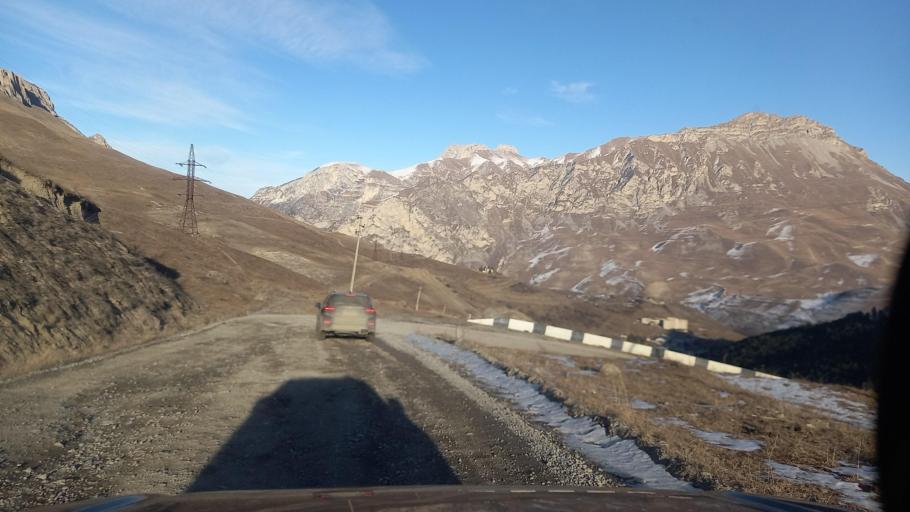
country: RU
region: North Ossetia
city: Verkhniy Fiagdon
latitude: 42.8346
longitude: 44.4887
